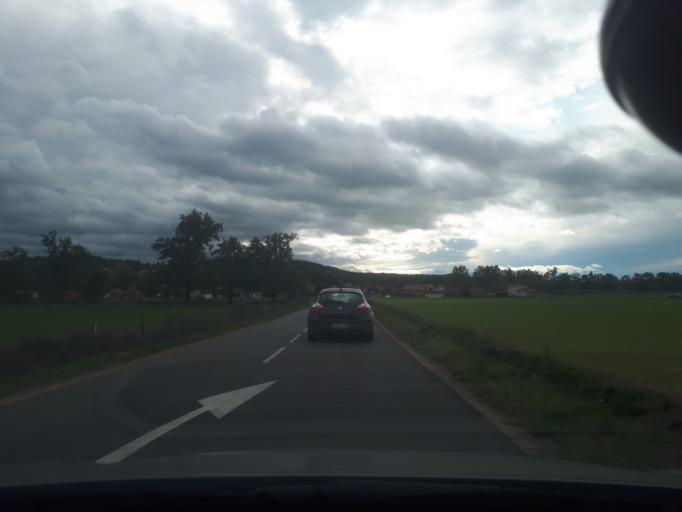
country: FR
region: Rhone-Alpes
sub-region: Departement de la Loire
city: Bellegarde-en-Forez
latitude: 45.7113
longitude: 4.2985
